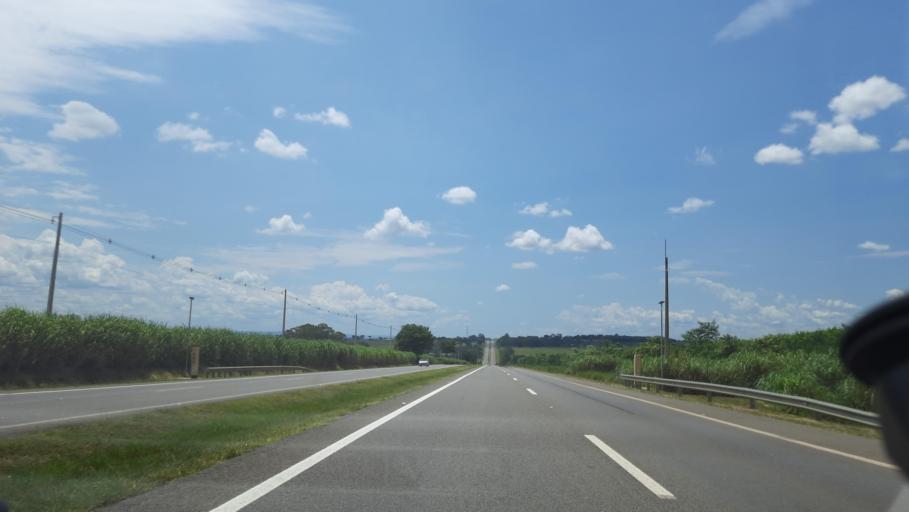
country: BR
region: Sao Paulo
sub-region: Mococa
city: Mococa
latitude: -21.5983
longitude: -47.0406
